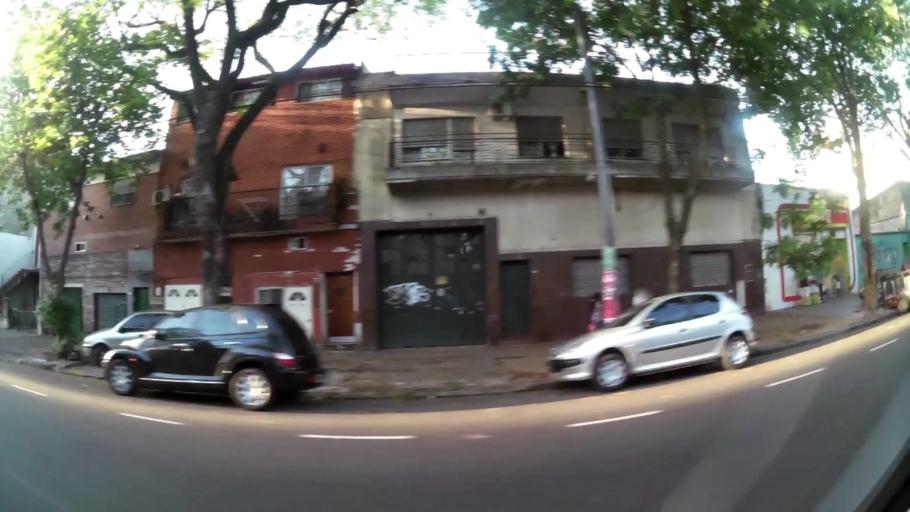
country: AR
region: Buenos Aires F.D.
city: Villa Lugano
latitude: -34.6425
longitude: -58.4359
